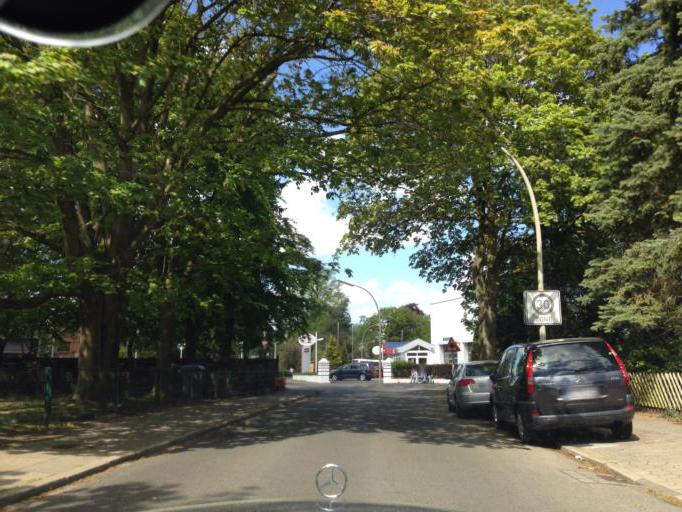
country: DE
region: Hamburg
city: Farmsen-Berne
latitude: 53.5938
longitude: 10.1461
